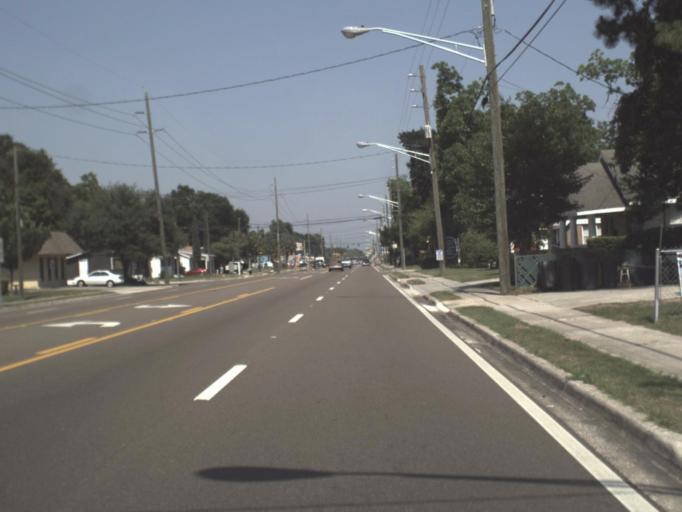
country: US
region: Florida
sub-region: Duval County
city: Jacksonville
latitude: 30.2821
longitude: -81.7335
